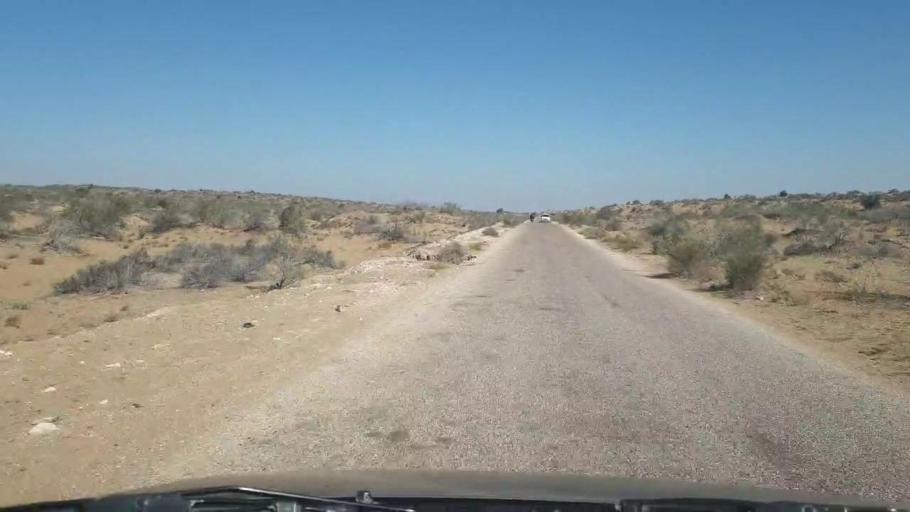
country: PK
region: Sindh
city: Bozdar
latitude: 27.0019
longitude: 68.8650
